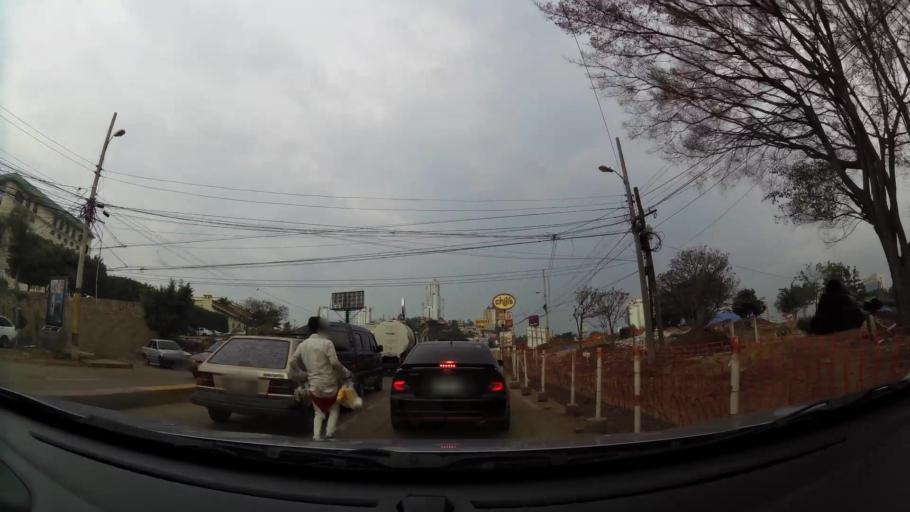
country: HN
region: Francisco Morazan
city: Tegucigalpa
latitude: 14.0893
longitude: -87.1944
